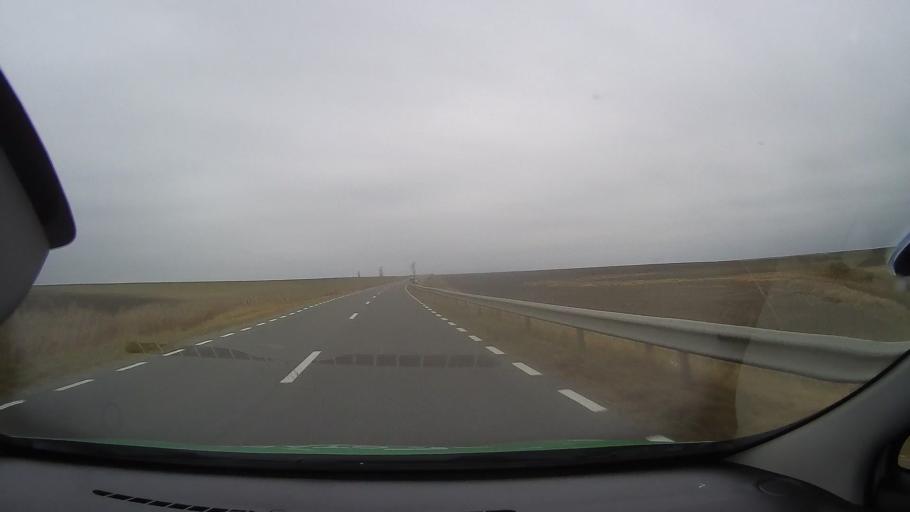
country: RO
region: Ialomita
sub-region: Comuna Scanteia
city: Iazu
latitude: 44.7205
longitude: 27.4216
